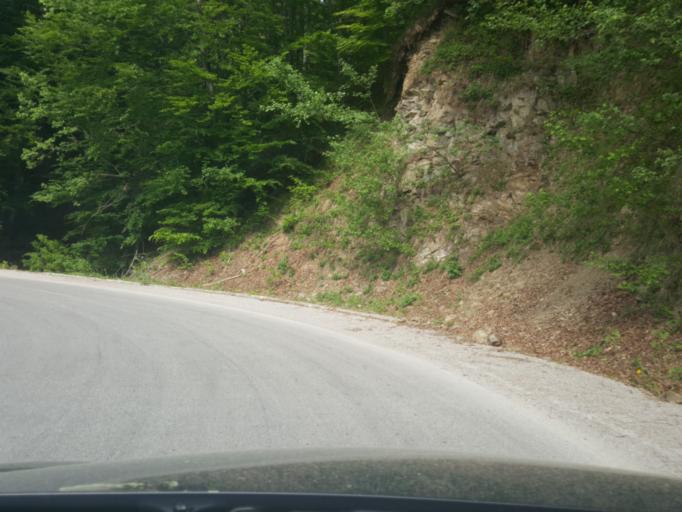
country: RS
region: Central Serbia
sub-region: Zlatiborski Okrug
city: Bajina Basta
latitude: 44.0751
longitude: 19.6633
